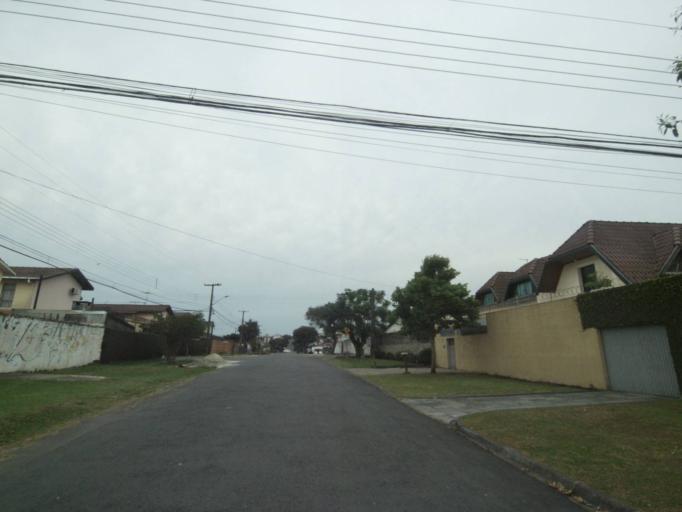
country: BR
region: Parana
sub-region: Pinhais
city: Pinhais
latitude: -25.4116
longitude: -49.2002
